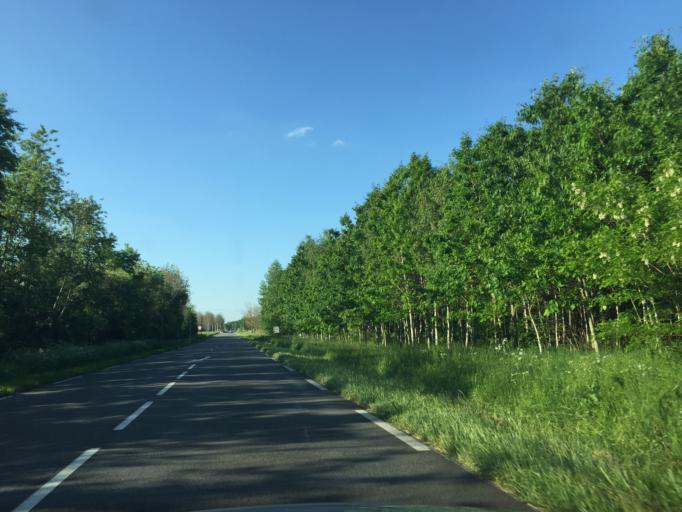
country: FR
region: Poitou-Charentes
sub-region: Departement de la Charente
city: Chalais
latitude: 45.2146
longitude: 0.0330
